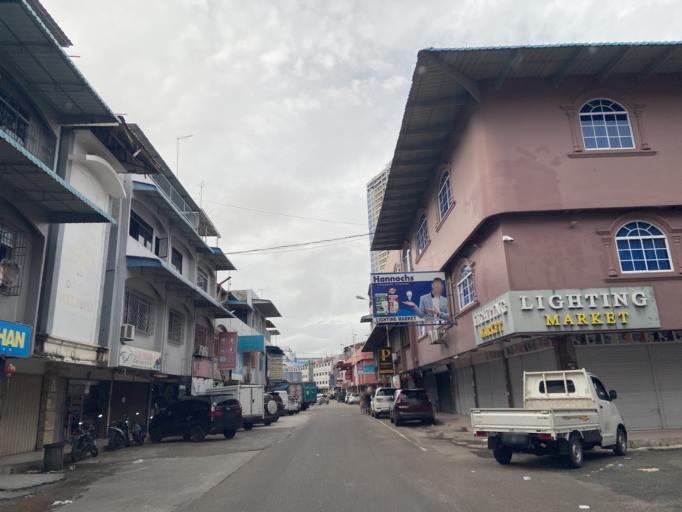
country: SG
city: Singapore
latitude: 1.1469
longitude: 104.0093
